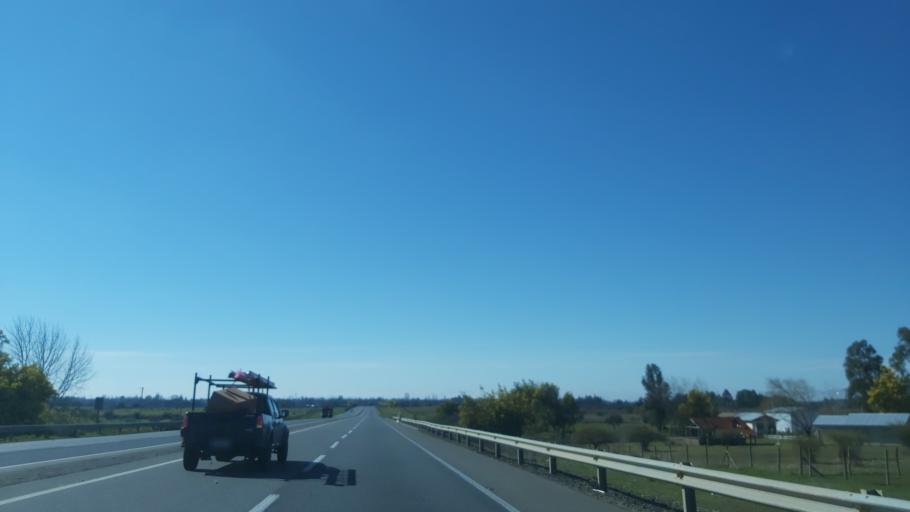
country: CL
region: Biobio
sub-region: Provincia de Nuble
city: Bulnes
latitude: -36.6583
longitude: -72.2508
